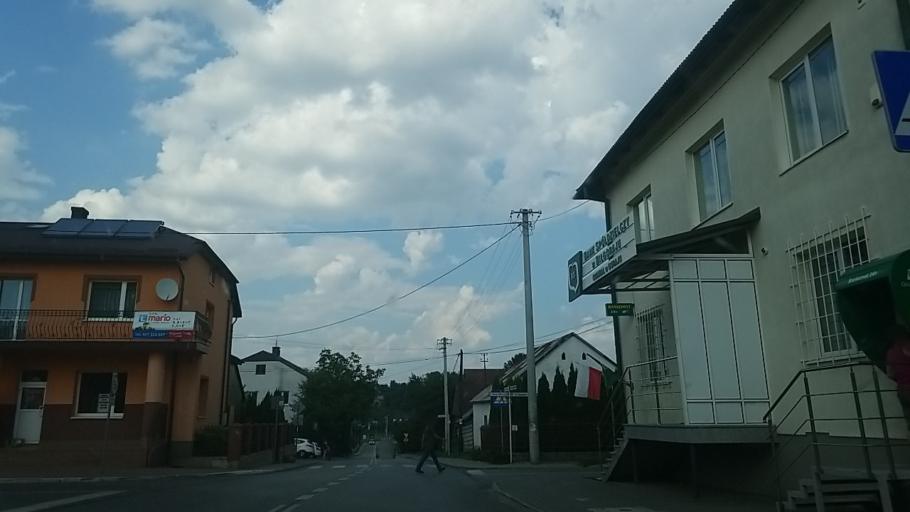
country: PL
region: Lublin Voivodeship
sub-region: Powiat bilgorajski
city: Goraj
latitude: 50.7215
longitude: 22.6675
